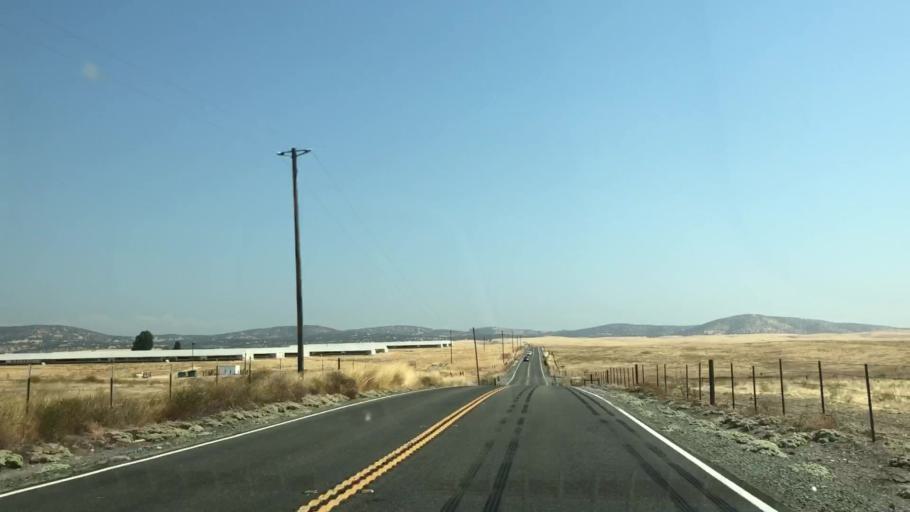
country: US
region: California
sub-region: Stanislaus County
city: East Oakdale
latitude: 37.9374
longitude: -120.8087
